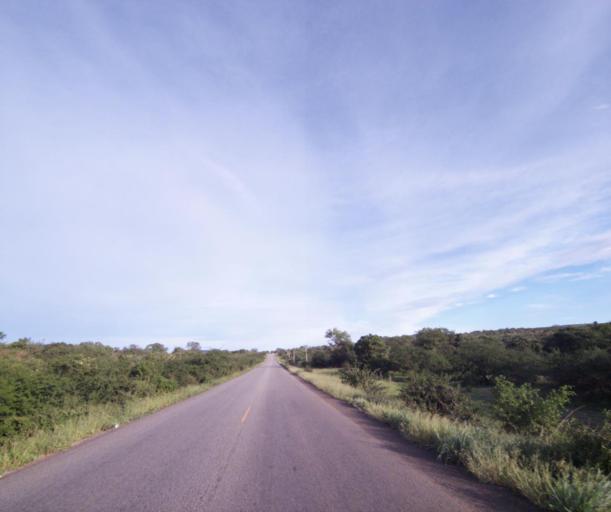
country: BR
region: Bahia
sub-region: Caetite
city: Caetite
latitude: -14.1753
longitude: -42.1798
